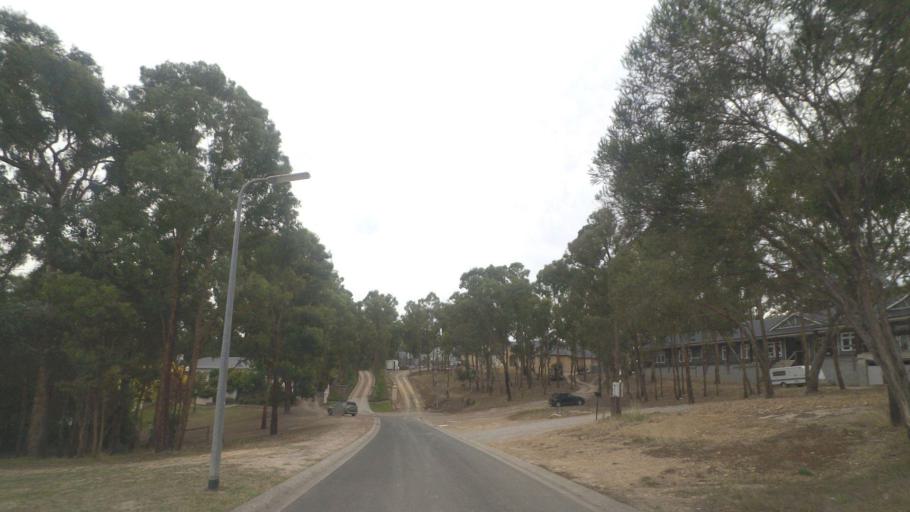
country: AU
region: Victoria
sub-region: Nillumbik
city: North Warrandyte
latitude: -37.7433
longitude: 145.1913
